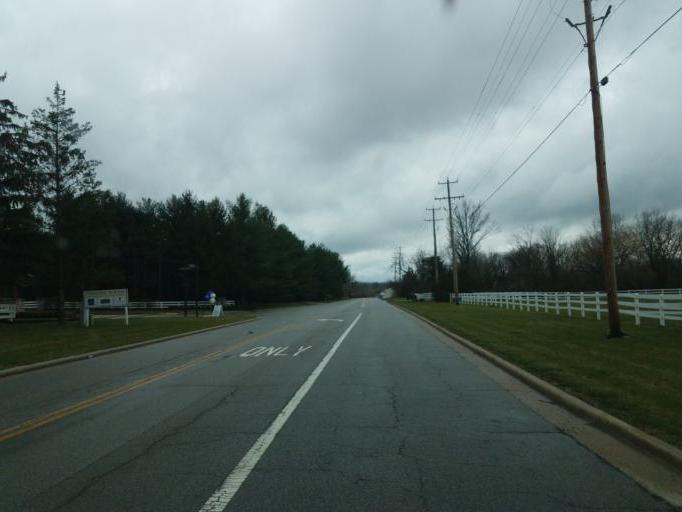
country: US
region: Ohio
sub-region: Delaware County
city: Sunbury
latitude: 40.2427
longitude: -82.9227
